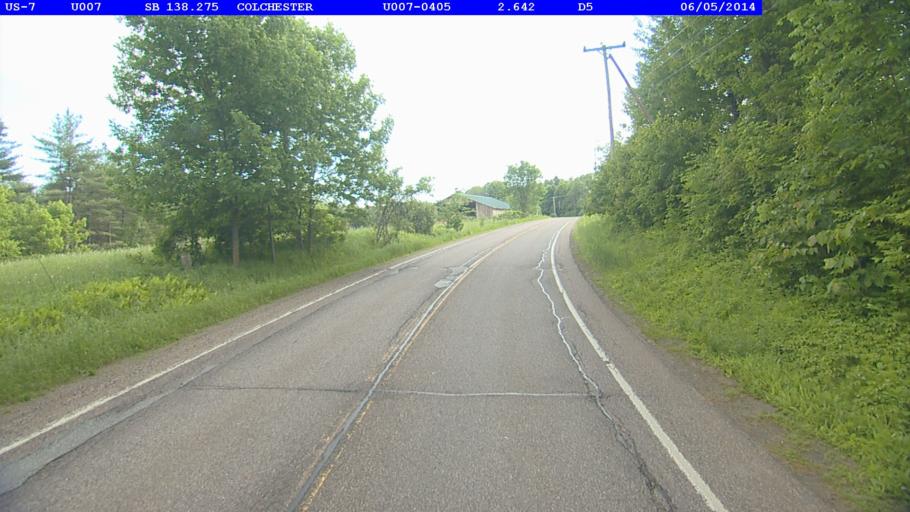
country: US
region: Vermont
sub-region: Chittenden County
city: Colchester
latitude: 44.5375
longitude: -73.1682
